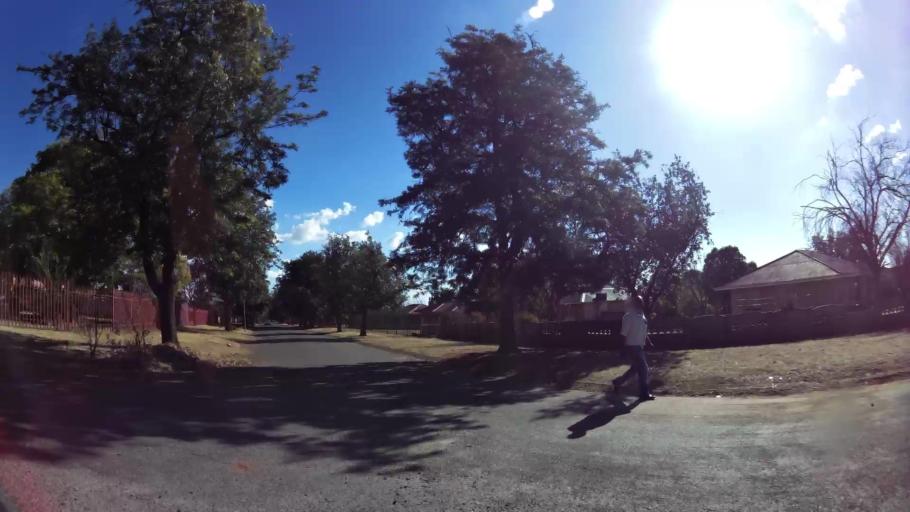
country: ZA
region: Gauteng
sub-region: West Rand District Municipality
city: Carletonville
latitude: -26.3735
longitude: 27.4040
